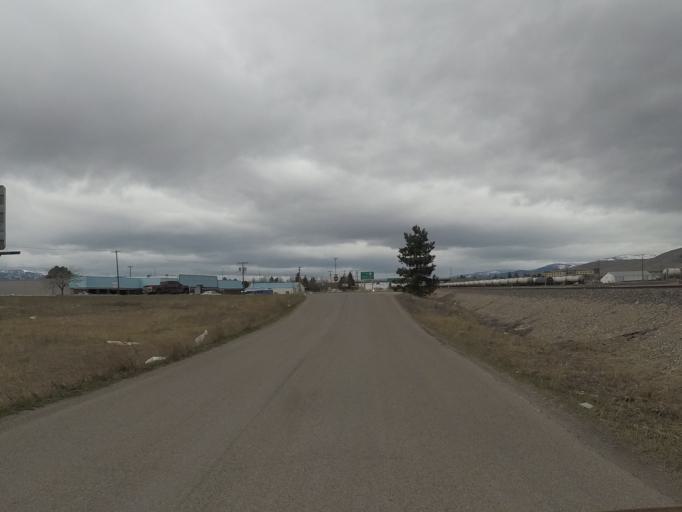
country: US
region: Montana
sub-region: Missoula County
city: Orchard Homes
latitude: 46.8955
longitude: -114.0325
